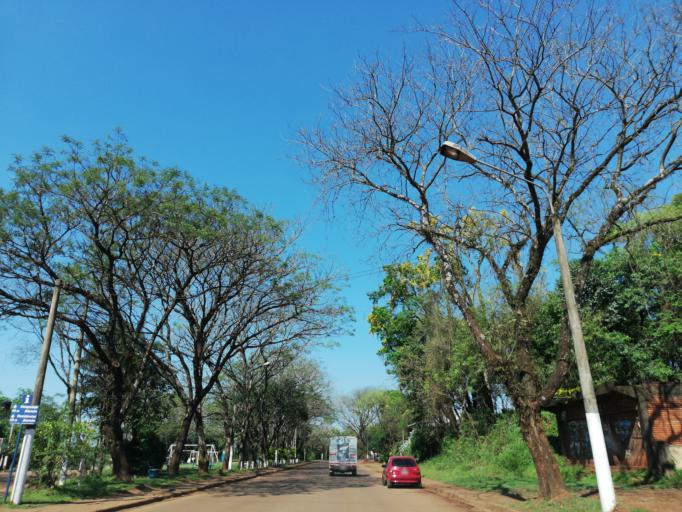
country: AR
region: Misiones
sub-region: Departamento de Eldorado
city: Eldorado
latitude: -26.4068
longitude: -54.6408
